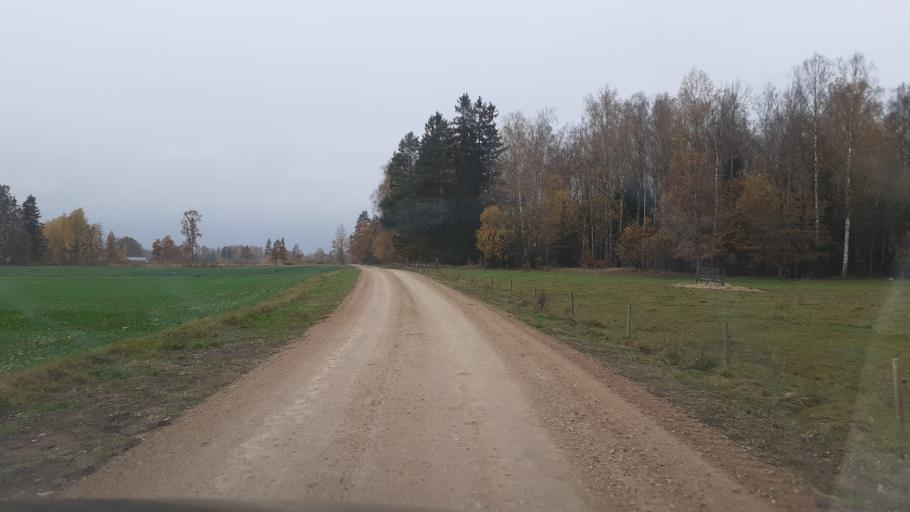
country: LV
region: Saldus Rajons
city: Saldus
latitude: 56.8724
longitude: 22.3290
